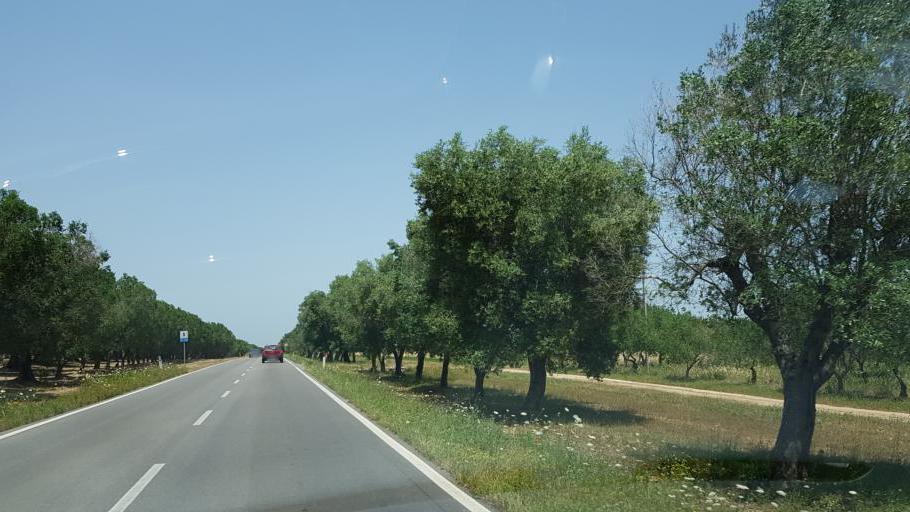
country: IT
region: Apulia
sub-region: Provincia di Brindisi
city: San Pancrazio Salentino
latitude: 40.3609
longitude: 17.8426
